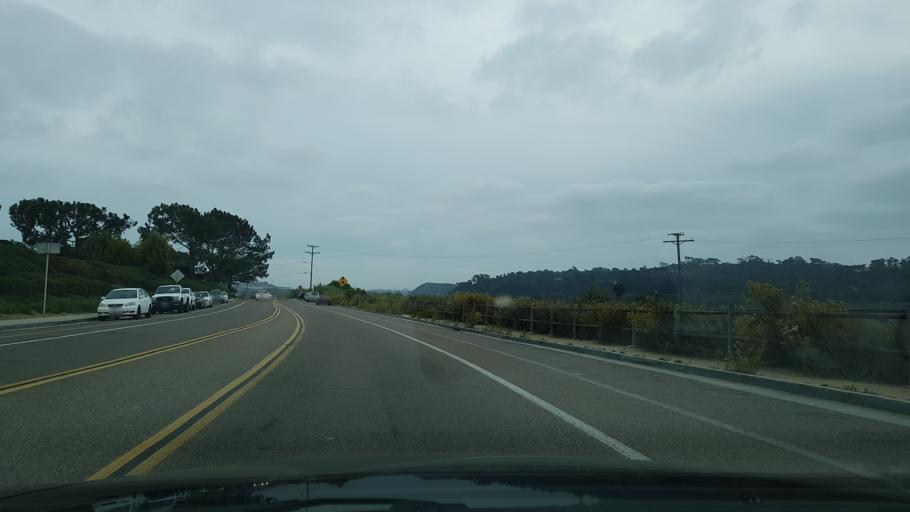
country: US
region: California
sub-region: San Diego County
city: Del Mar
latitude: 32.9355
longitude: -117.2570
